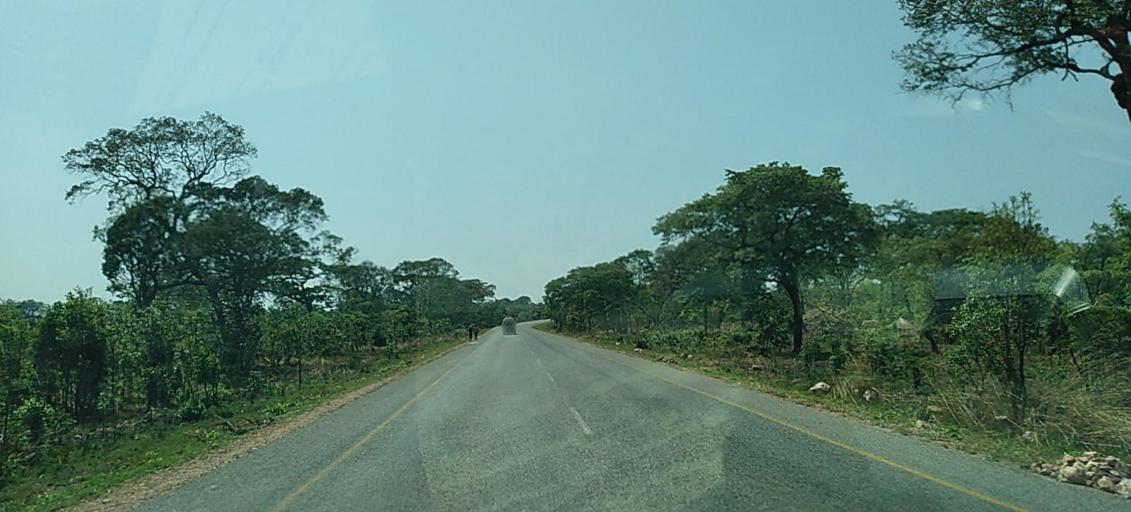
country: ZM
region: North-Western
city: Solwezi
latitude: -12.2856
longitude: 25.7843
